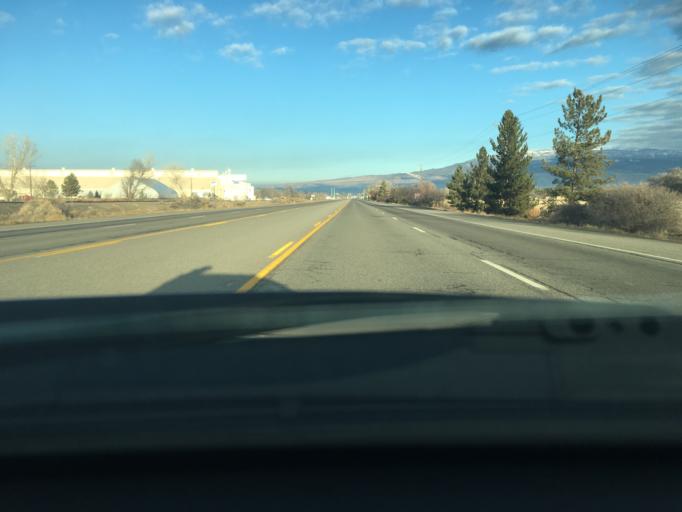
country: US
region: Colorado
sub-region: Delta County
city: Delta
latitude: 38.7210
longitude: -108.0594
